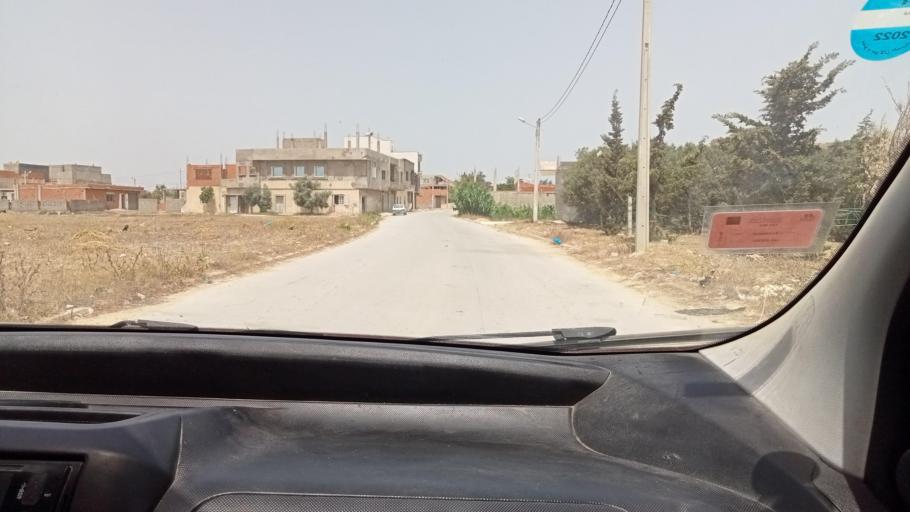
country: TN
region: Nabul
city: Qulaybiyah
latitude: 36.8621
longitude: 11.0862
